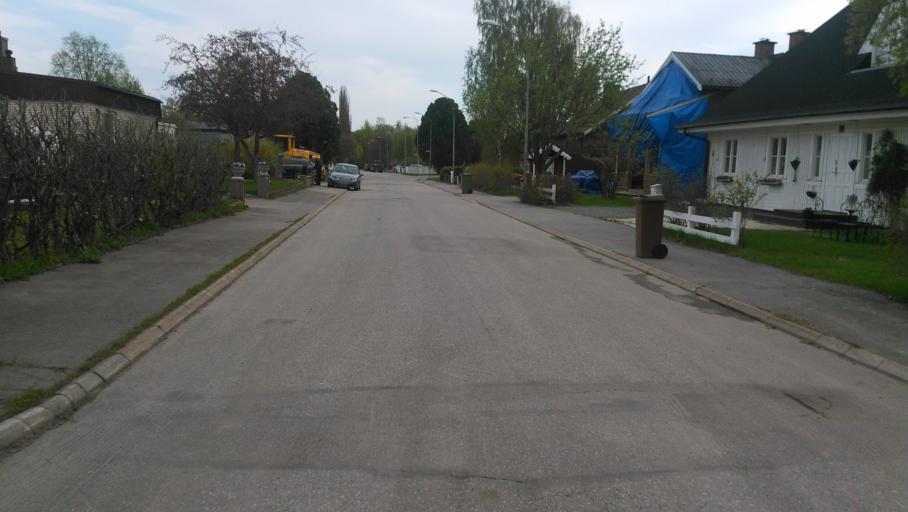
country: SE
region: Vaesterbotten
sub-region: Umea Kommun
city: Umea
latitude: 63.8116
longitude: 20.2690
